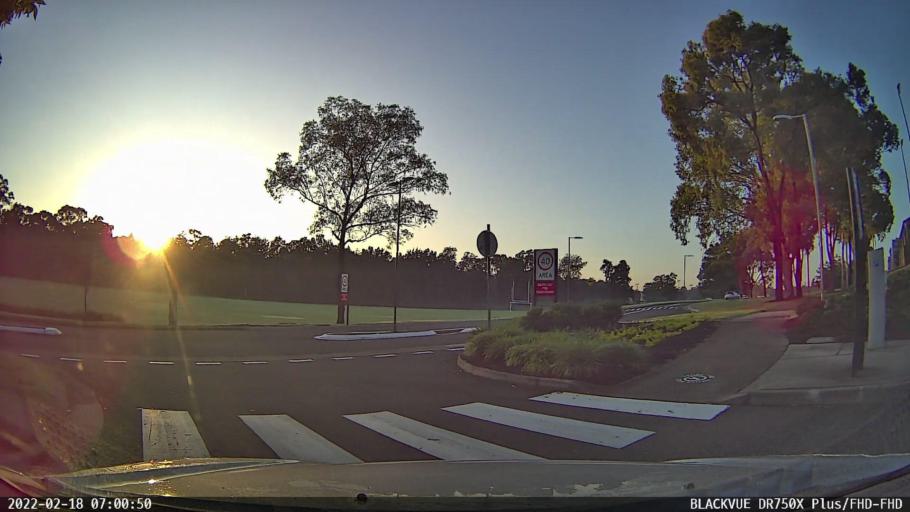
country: AU
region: New South Wales
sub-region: Penrith Municipality
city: Kingswood Park
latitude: -33.7649
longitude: 150.7305
